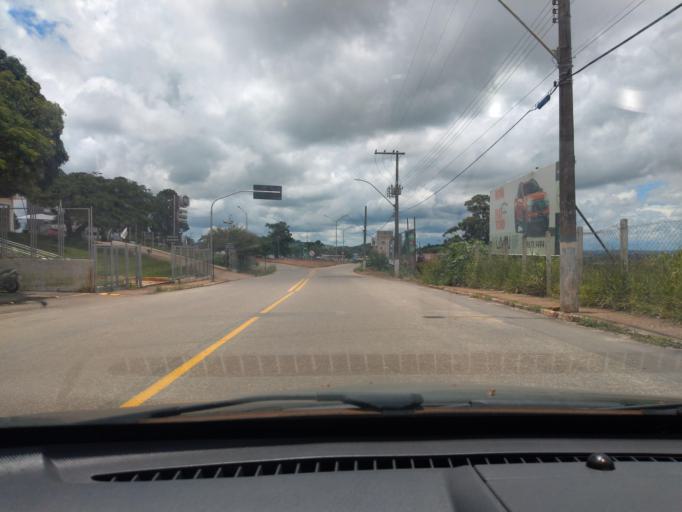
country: BR
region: Minas Gerais
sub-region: Lavras
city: Lavras
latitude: -21.2392
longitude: -45.0240
